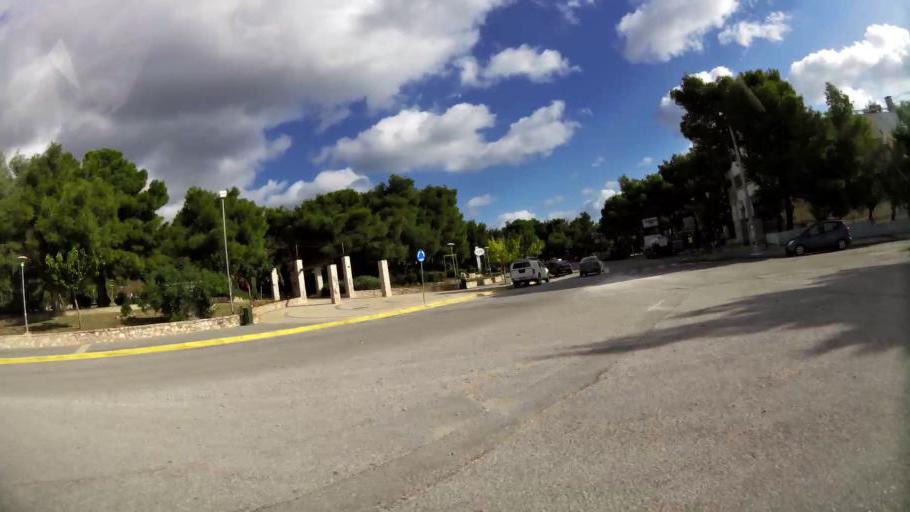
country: GR
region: Attica
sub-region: Nomarchia Anatolikis Attikis
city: Thrakomakedones
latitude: 38.1287
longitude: 23.7578
